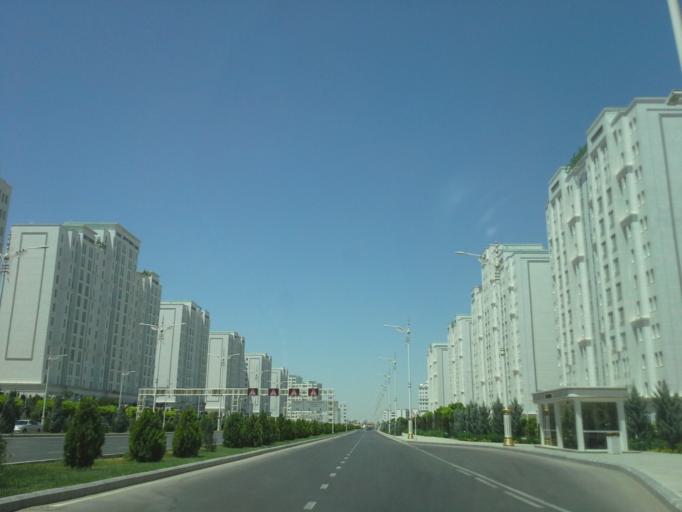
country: TM
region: Ahal
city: Ashgabat
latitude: 37.9313
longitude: 58.3687
